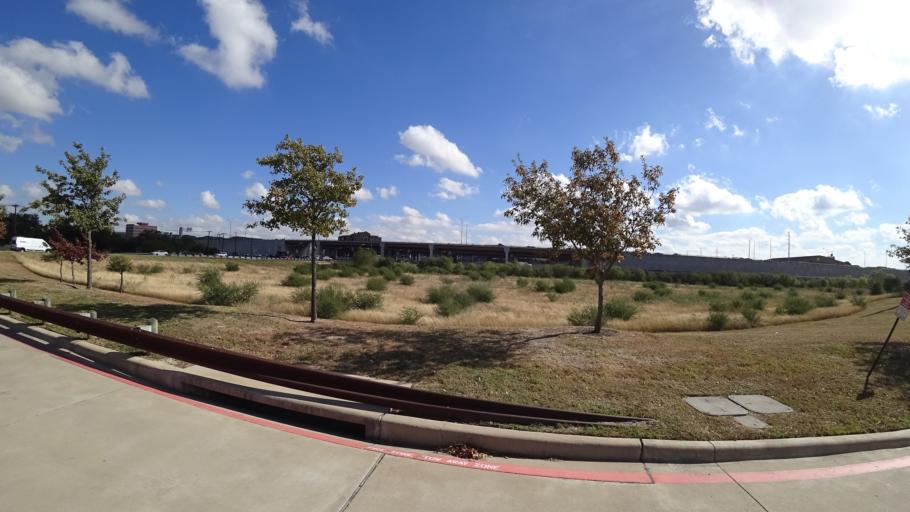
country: US
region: Texas
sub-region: Travis County
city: Wells Branch
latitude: 30.4401
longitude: -97.7005
